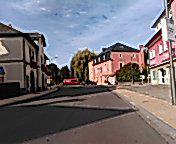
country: LU
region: Luxembourg
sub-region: Canton de Capellen
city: Steinfort
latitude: 49.6447
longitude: 5.9156
